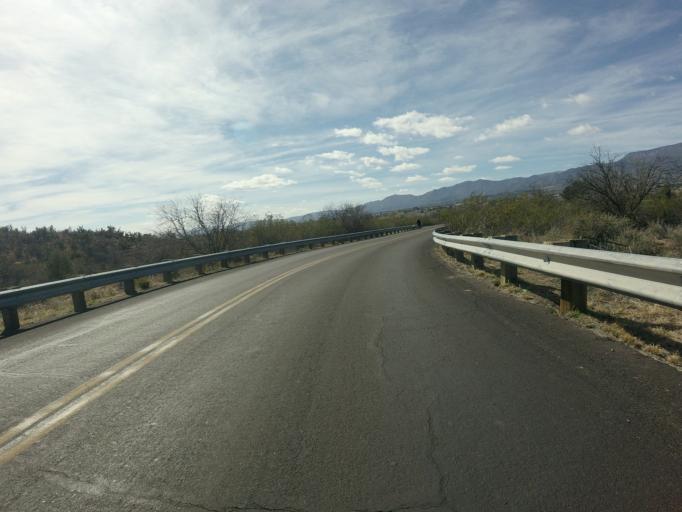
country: US
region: Arizona
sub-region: Yavapai County
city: Cottonwood
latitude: 34.7564
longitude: -112.0153
